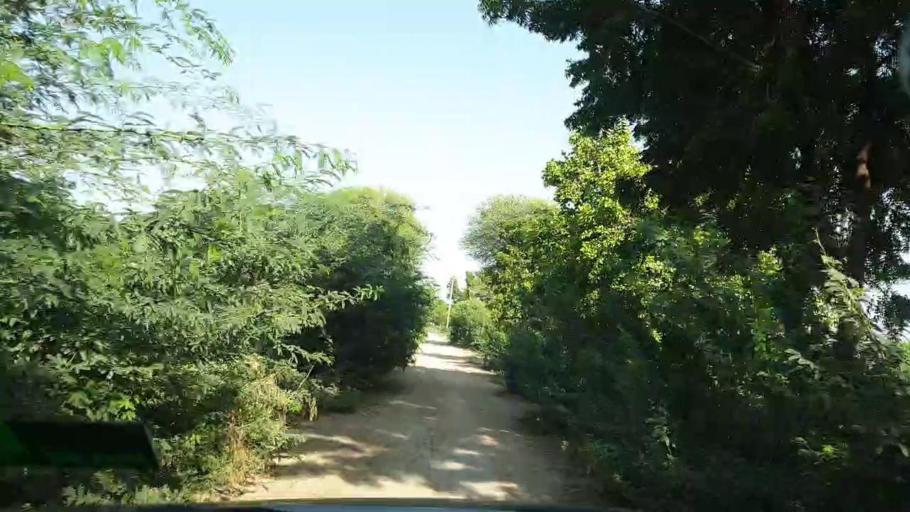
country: PK
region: Sindh
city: Naukot
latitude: 24.7030
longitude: 69.2192
